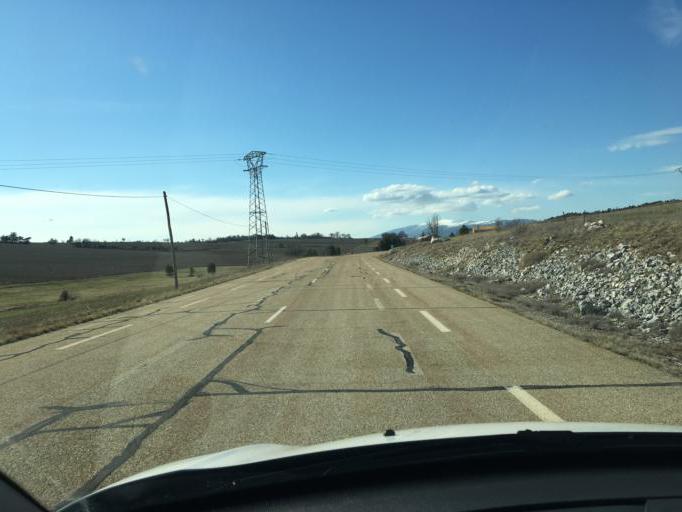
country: FR
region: Provence-Alpes-Cote d'Azur
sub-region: Departement du Vaucluse
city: Sault
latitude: 44.0301
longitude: 5.4601
